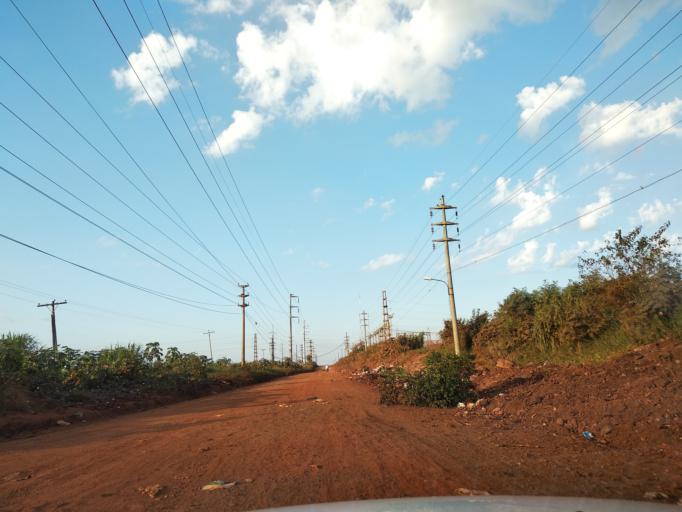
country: AR
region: Misiones
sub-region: Departamento de Capital
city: Posadas
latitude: -27.4398
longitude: -55.9159
